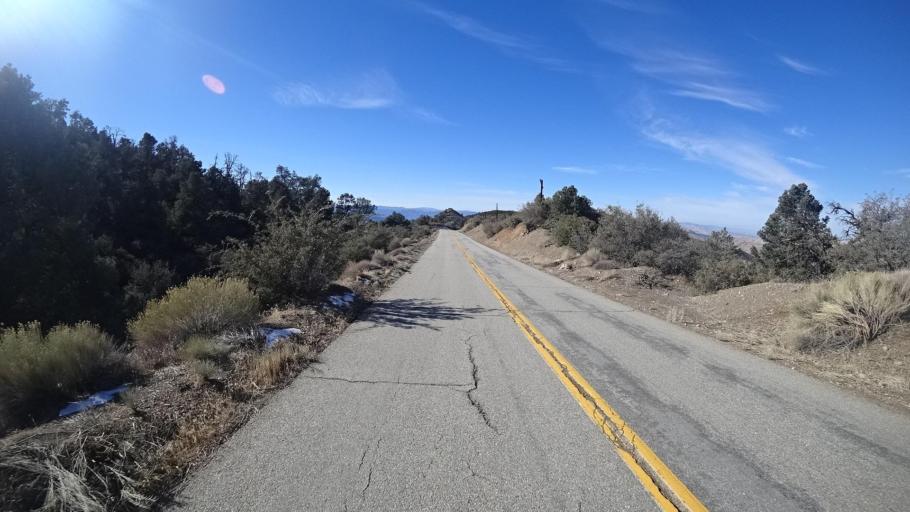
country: US
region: California
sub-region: Kern County
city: Pine Mountain Club
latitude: 34.8651
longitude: -119.2409
